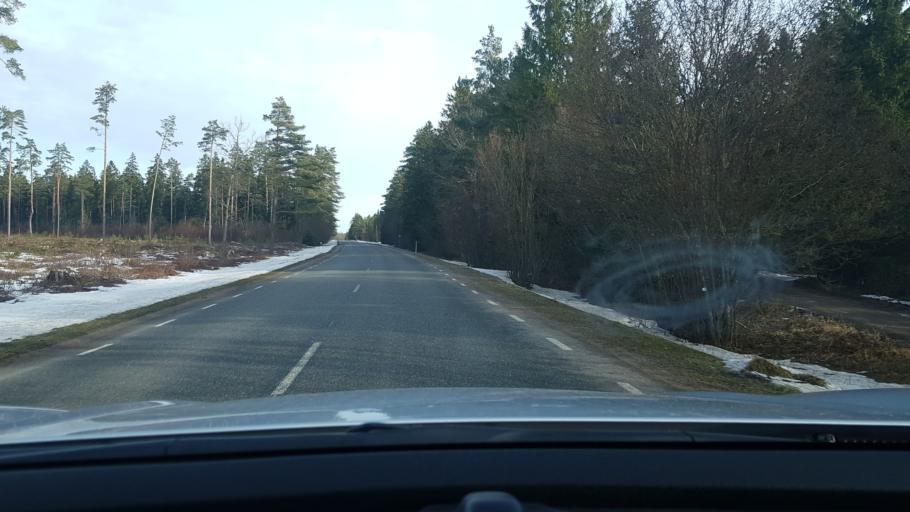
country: EE
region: Saare
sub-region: Kuressaare linn
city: Kuressaare
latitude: 58.4102
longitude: 22.6552
